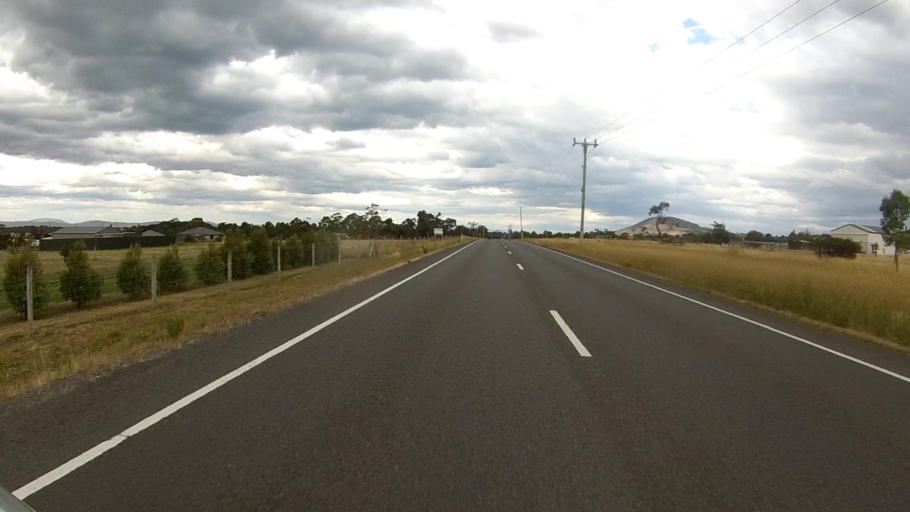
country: AU
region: Tasmania
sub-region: Clarence
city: Cambridge
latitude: -42.8408
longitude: 147.4693
